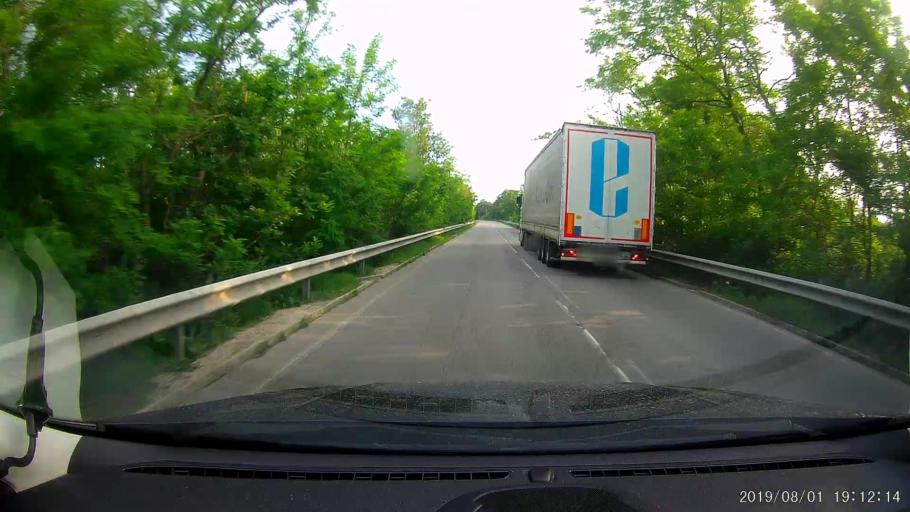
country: BG
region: Shumen
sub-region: Obshtina Smyadovo
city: Smyadovo
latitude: 42.9661
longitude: 26.9519
